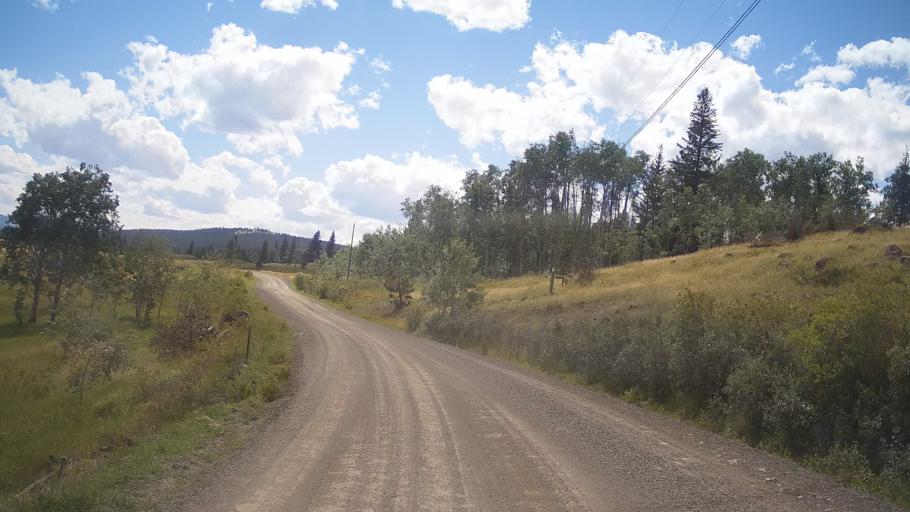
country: CA
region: British Columbia
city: Lillooet
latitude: 51.3260
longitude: -121.9796
